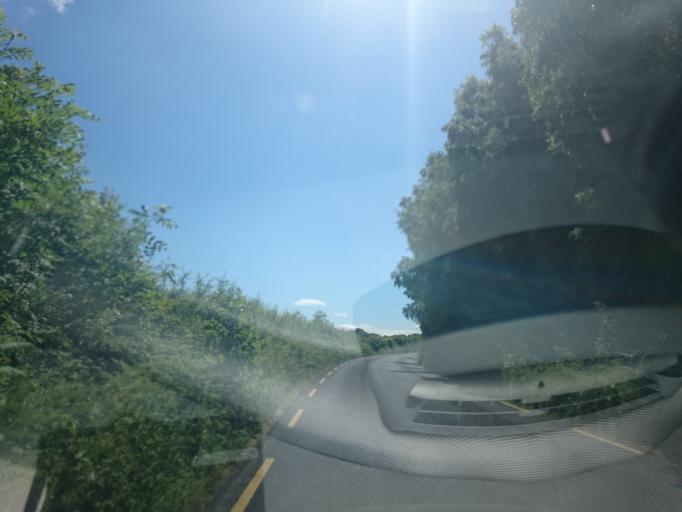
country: IE
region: Leinster
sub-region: Kilkenny
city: Graiguenamanagh
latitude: 52.5833
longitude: -6.9536
